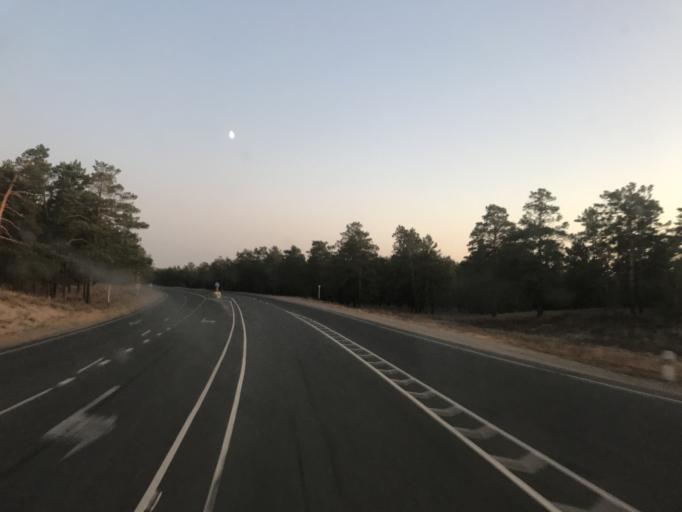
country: KZ
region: East Kazakhstan
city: Semey
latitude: 50.5072
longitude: 80.1091
